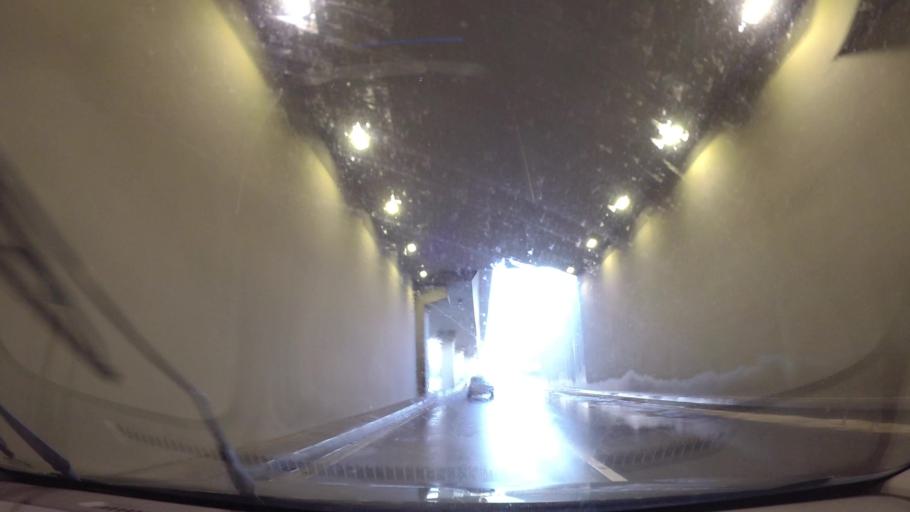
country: JO
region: Amman
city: Al Jubayhah
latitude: 31.9923
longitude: 35.8905
